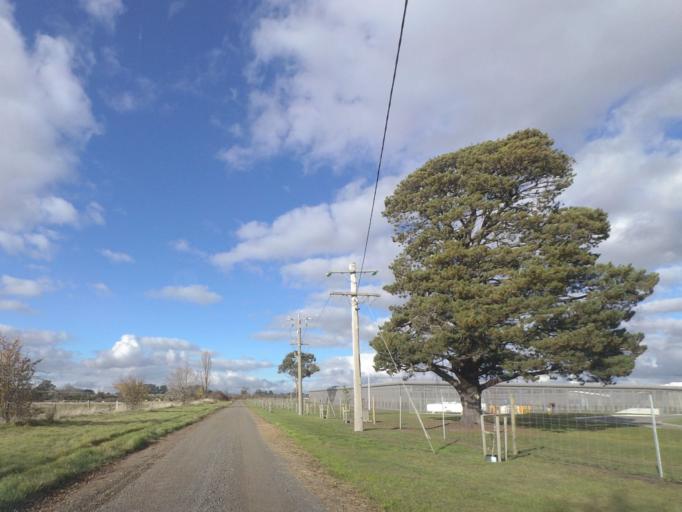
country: AU
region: Victoria
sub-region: Mount Alexander
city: Castlemaine
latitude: -37.1857
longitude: 144.3967
